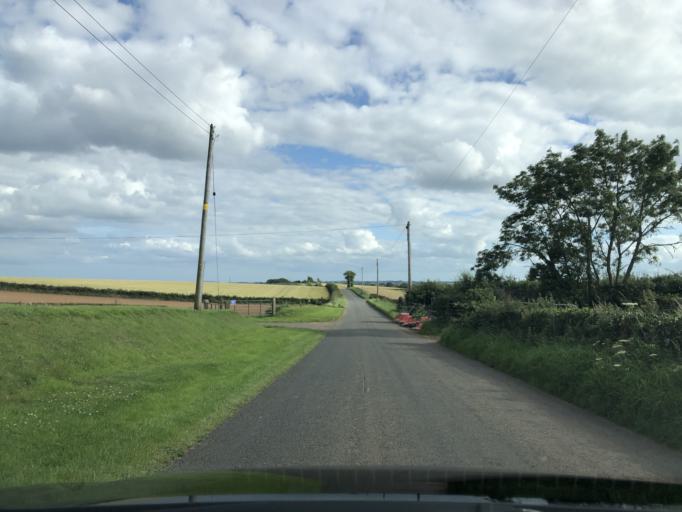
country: GB
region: Northern Ireland
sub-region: Ards District
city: Newtownards
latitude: 54.5673
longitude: -5.7125
